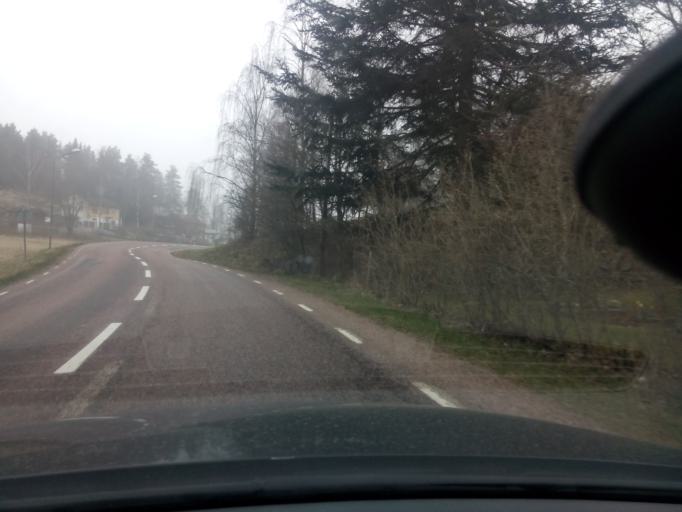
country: SE
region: Soedermanland
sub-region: Nykopings Kommun
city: Nykoping
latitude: 58.8735
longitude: 17.0766
